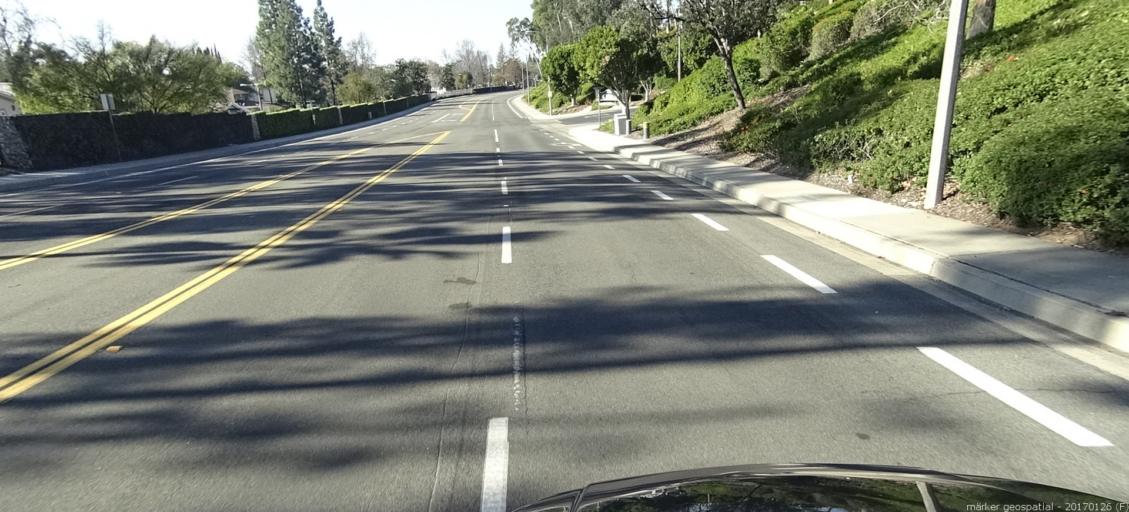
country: US
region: California
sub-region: Orange County
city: Lake Forest
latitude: 33.6439
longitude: -117.6990
